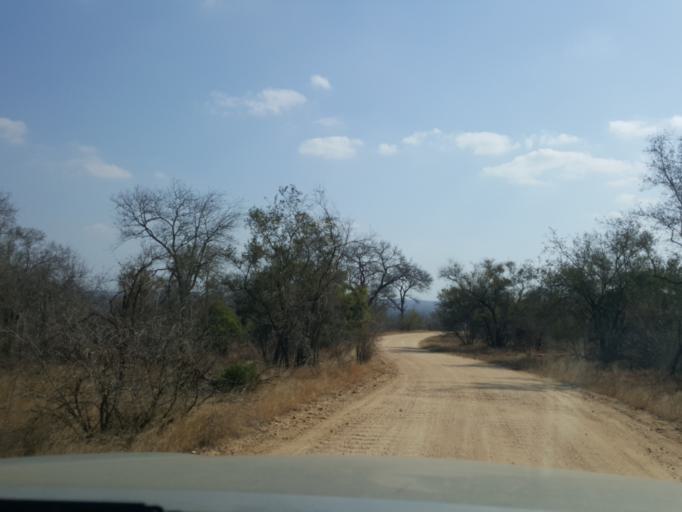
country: ZA
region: Mpumalanga
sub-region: Ehlanzeni District
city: Komatipoort
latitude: -25.2729
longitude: 31.7897
